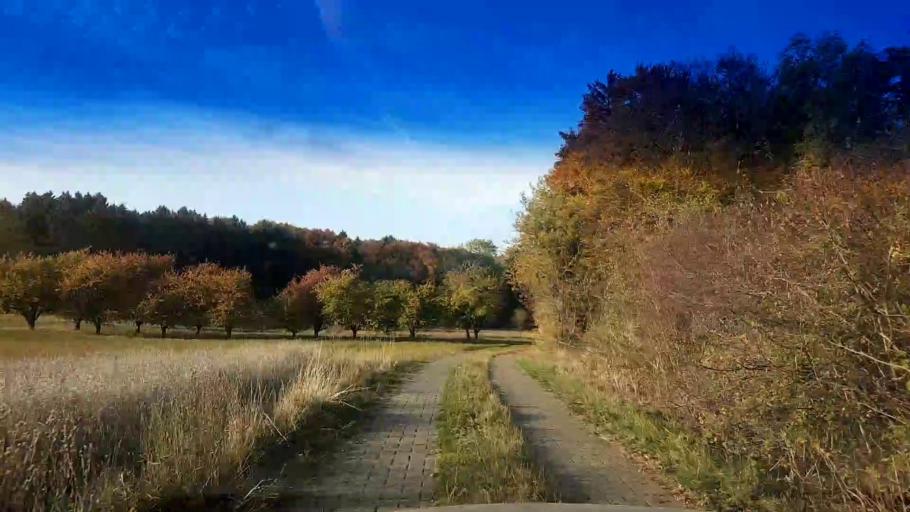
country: DE
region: Bavaria
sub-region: Upper Franconia
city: Poxdorf
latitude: 49.9329
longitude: 11.0728
